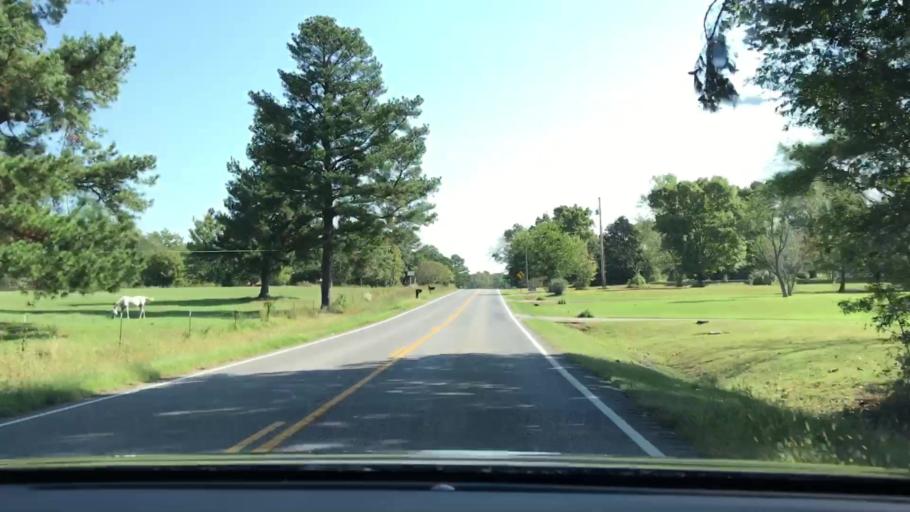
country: US
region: Kentucky
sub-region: Marshall County
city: Benton
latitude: 36.7638
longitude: -88.2007
